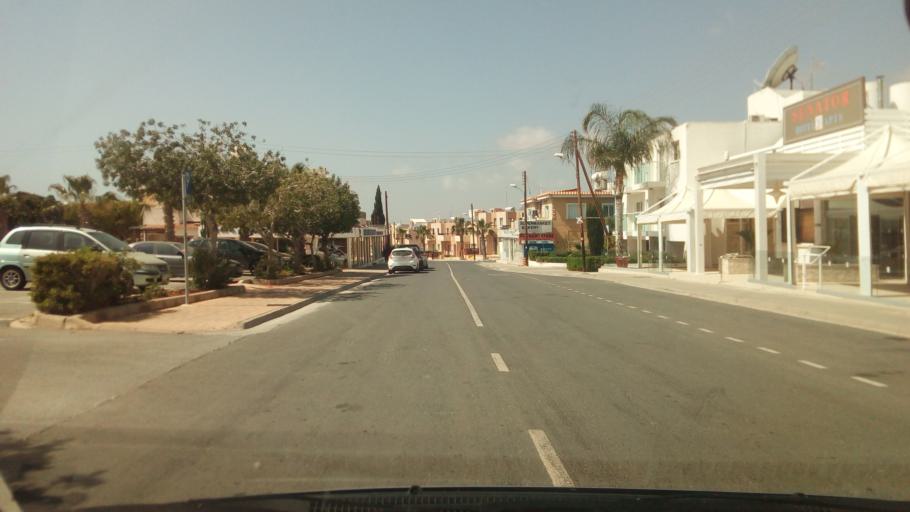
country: CY
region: Ammochostos
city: Ayia Napa
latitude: 34.9917
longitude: 33.9949
